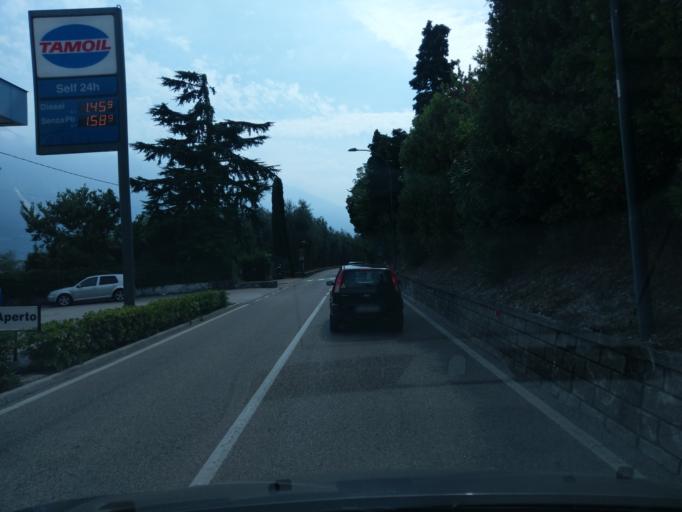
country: IT
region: Lombardy
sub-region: Provincia di Brescia
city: Limone sul Garda
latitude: 45.8052
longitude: 10.7874
